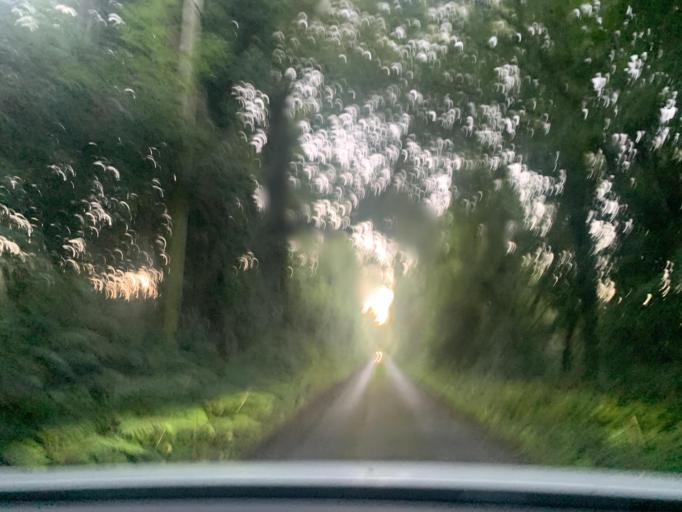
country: IE
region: Connaught
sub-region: Sligo
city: Sligo
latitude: 54.2745
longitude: -8.4170
